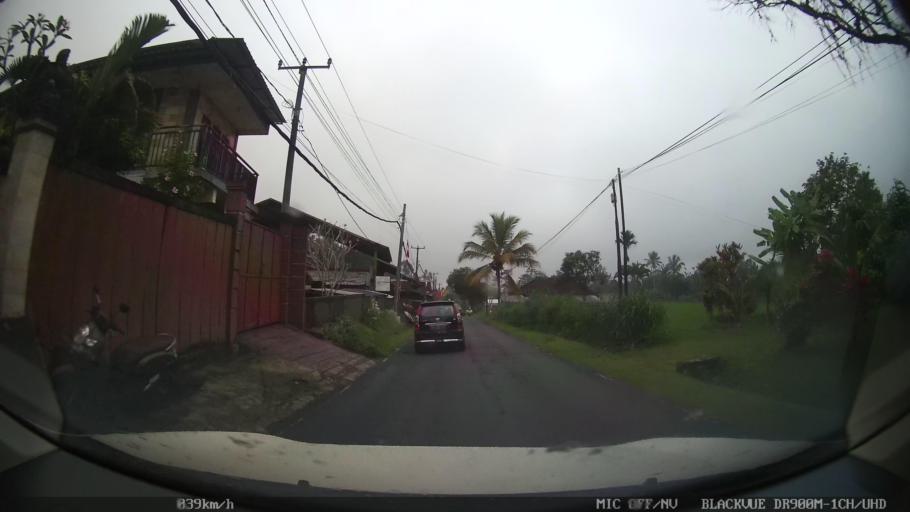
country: ID
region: Bali
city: Banjar Ponggang
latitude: -8.3769
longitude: 115.2673
